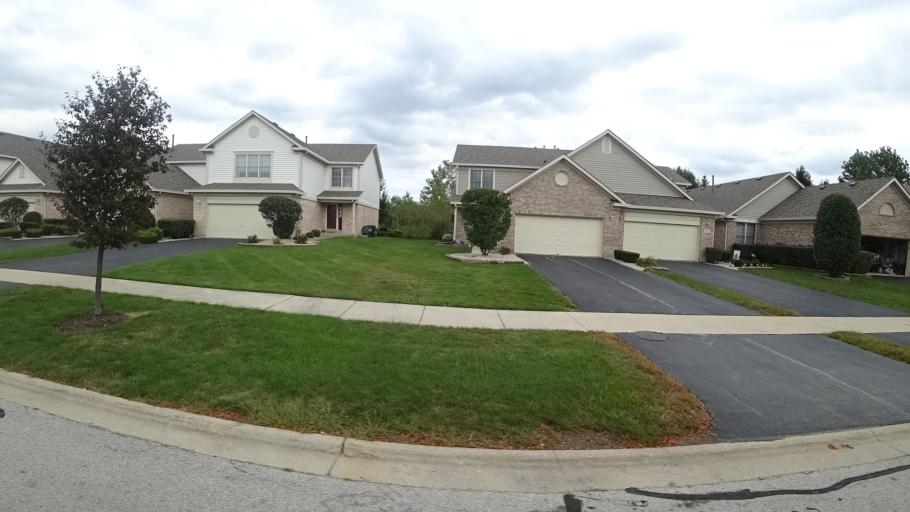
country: US
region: Illinois
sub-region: Cook County
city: Tinley Park
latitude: 41.5708
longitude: -87.8043
